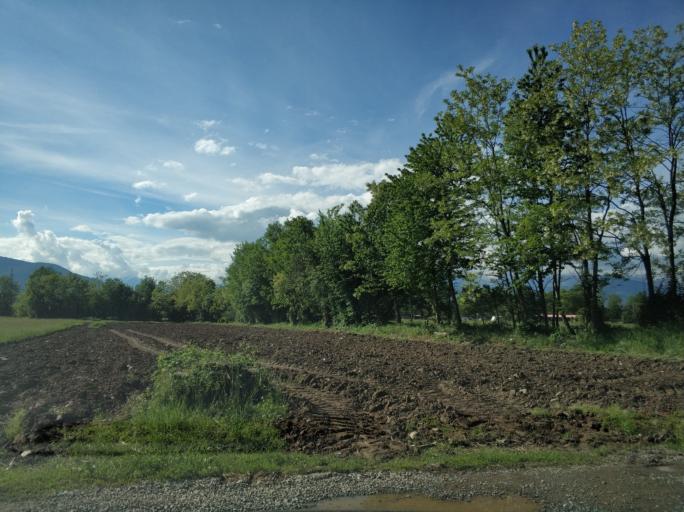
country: IT
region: Piedmont
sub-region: Provincia di Torino
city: Nole
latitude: 45.2287
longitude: 7.5733
